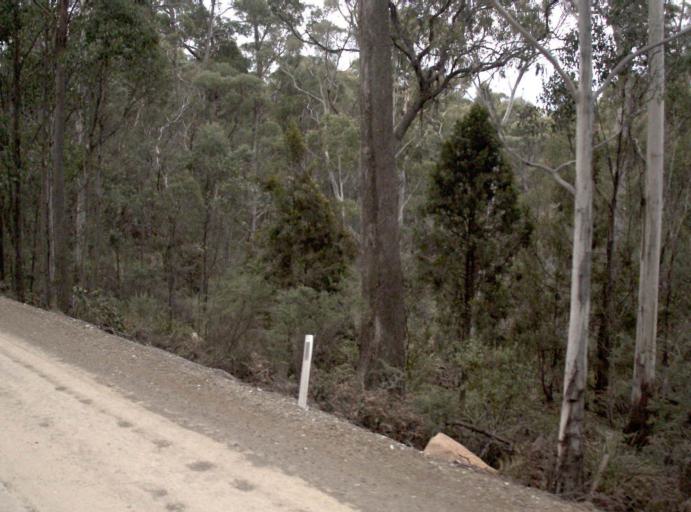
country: AU
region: Tasmania
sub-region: Launceston
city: Mayfield
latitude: -41.3379
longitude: 147.2081
